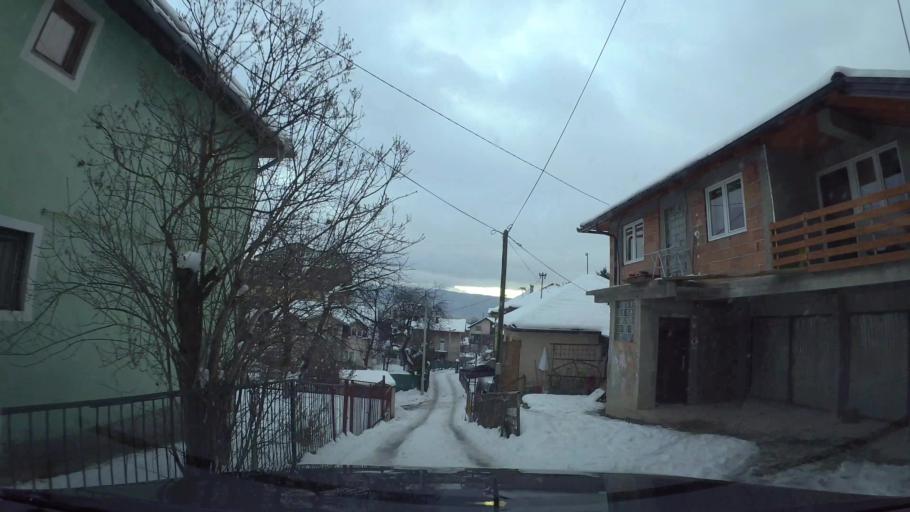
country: BA
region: Federation of Bosnia and Herzegovina
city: Kobilja Glava
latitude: 43.8607
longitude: 18.3877
